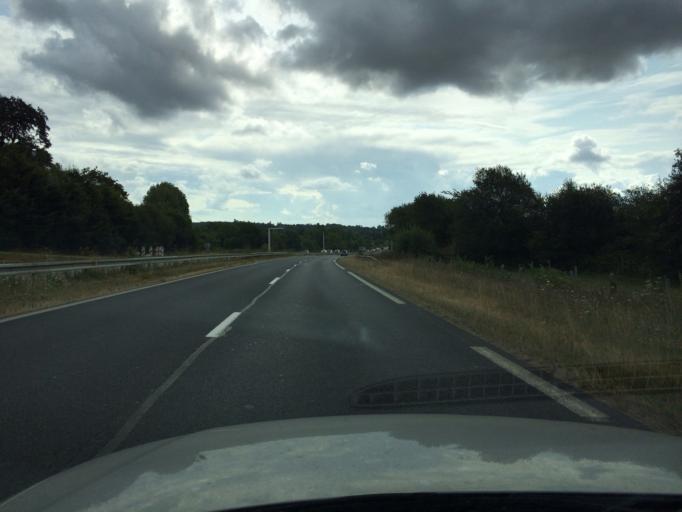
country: FR
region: Lower Normandy
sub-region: Departement de la Manche
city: Brix
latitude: 49.5315
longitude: -1.5246
